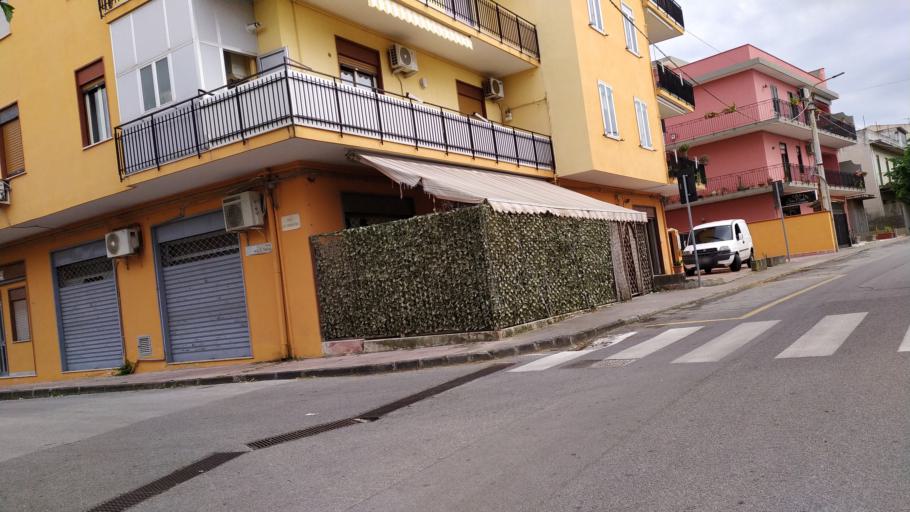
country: IT
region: Sicily
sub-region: Messina
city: San Filippo del Mela
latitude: 38.1819
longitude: 15.2707
